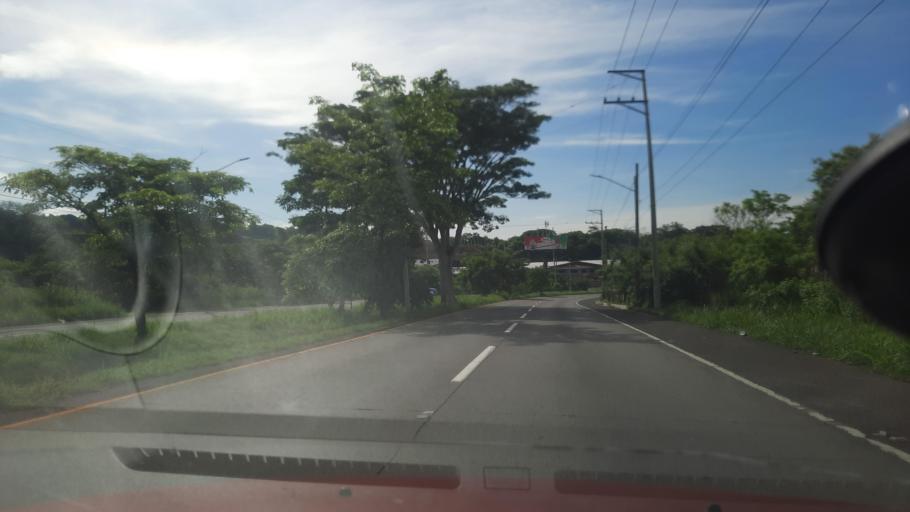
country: SV
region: La Paz
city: Olocuilta
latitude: 13.5246
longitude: -89.1070
